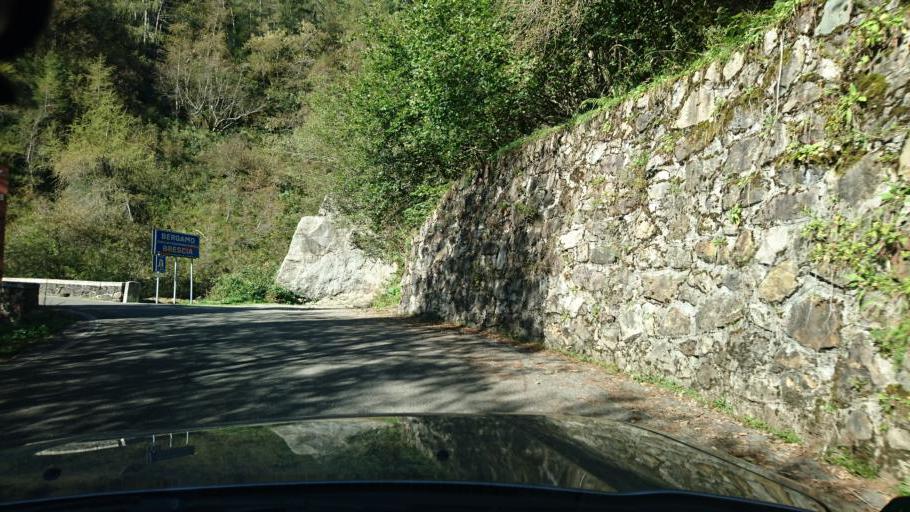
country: IT
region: Lombardy
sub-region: Provincia di Brescia
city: Lozio
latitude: 46.0498
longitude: 10.2231
